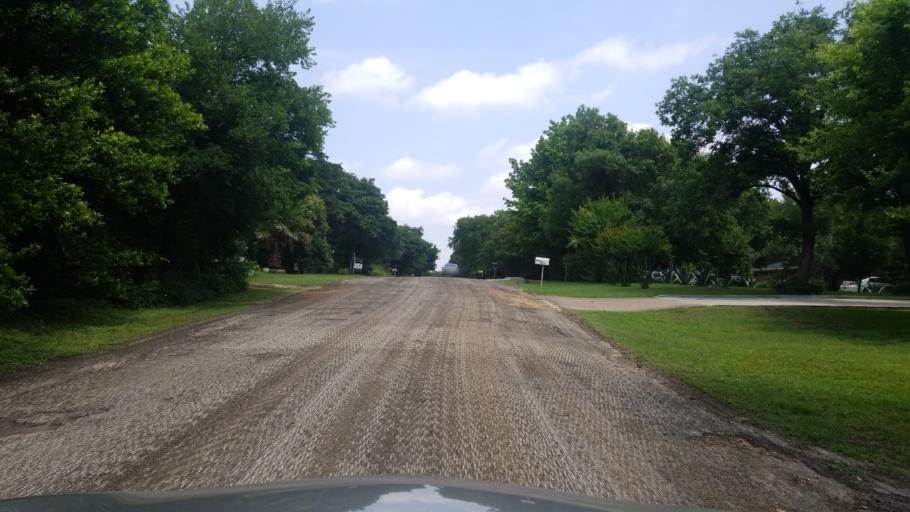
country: US
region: Texas
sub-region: Dallas County
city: Duncanville
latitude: 32.6803
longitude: -96.9154
